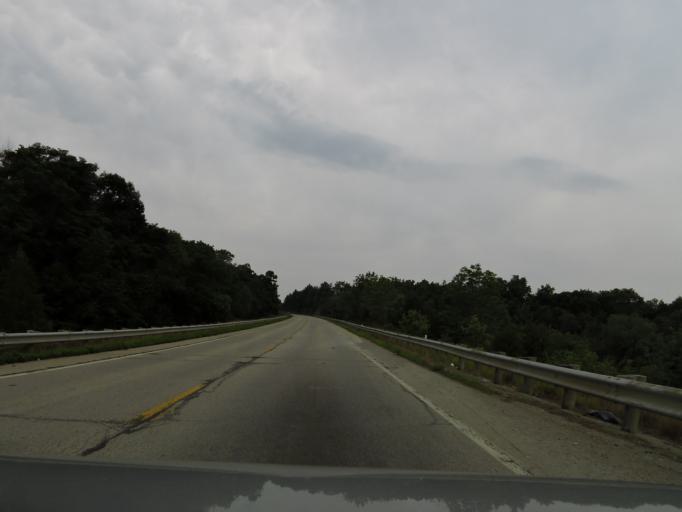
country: US
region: Ohio
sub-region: Brown County
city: Georgetown
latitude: 38.8361
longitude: -83.8405
